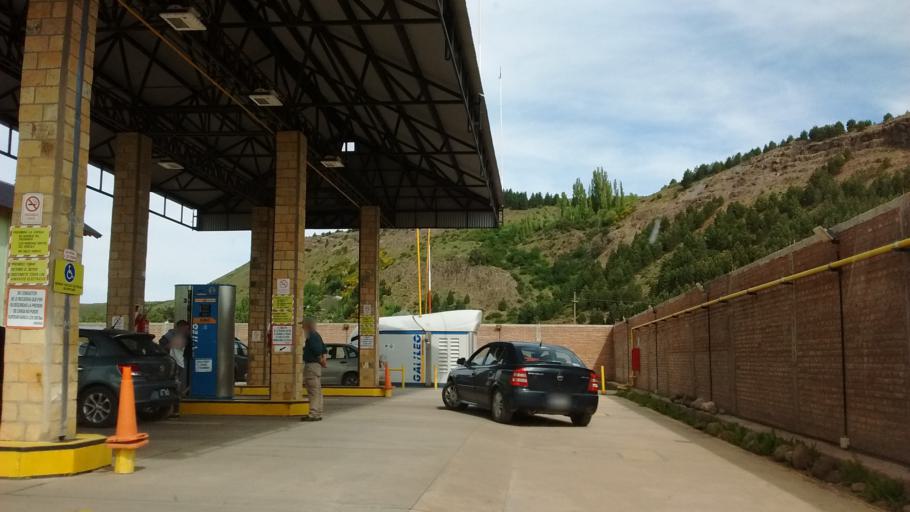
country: AR
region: Neuquen
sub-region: Departamento de Lacar
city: San Martin de los Andes
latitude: -40.1269
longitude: -71.2530
